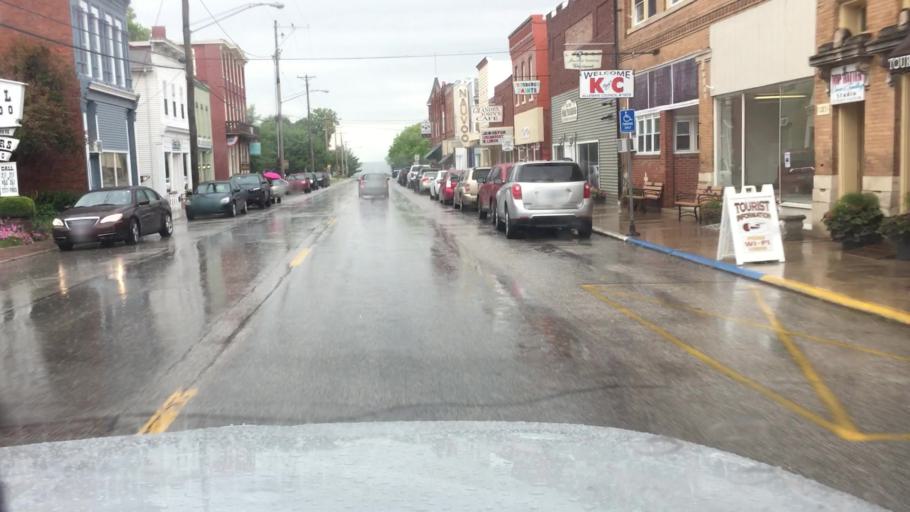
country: US
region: Illinois
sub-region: Hancock County
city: Nauvoo
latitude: 40.5498
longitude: -91.3819
